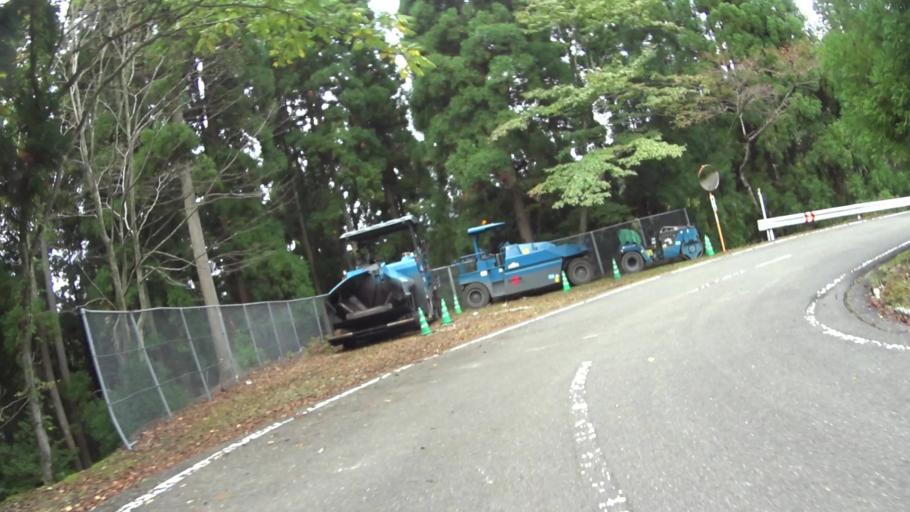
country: JP
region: Shiga Prefecture
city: Kitahama
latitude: 35.2742
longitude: 135.7260
